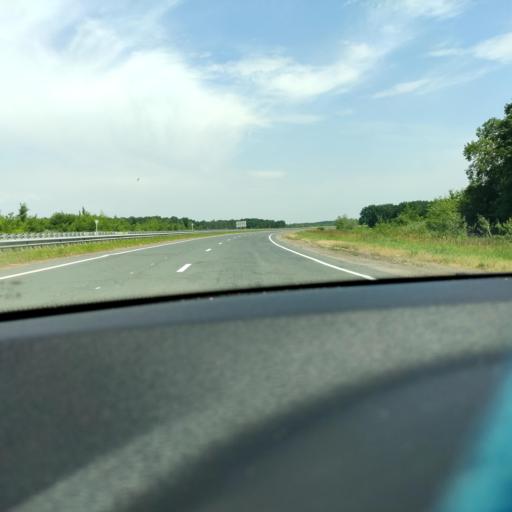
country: RU
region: Samara
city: Petra-Dubrava
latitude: 53.3385
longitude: 50.4347
